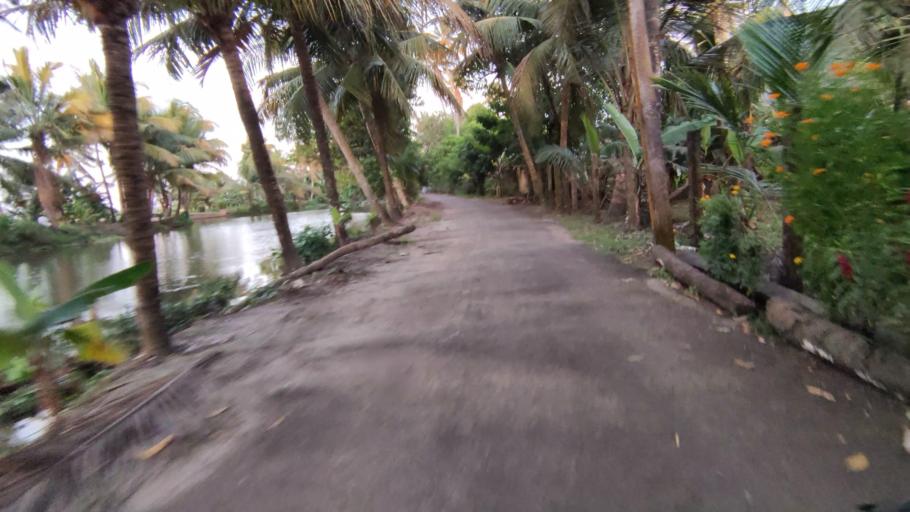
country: IN
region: Kerala
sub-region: Kottayam
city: Kottayam
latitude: 9.5761
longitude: 76.4535
